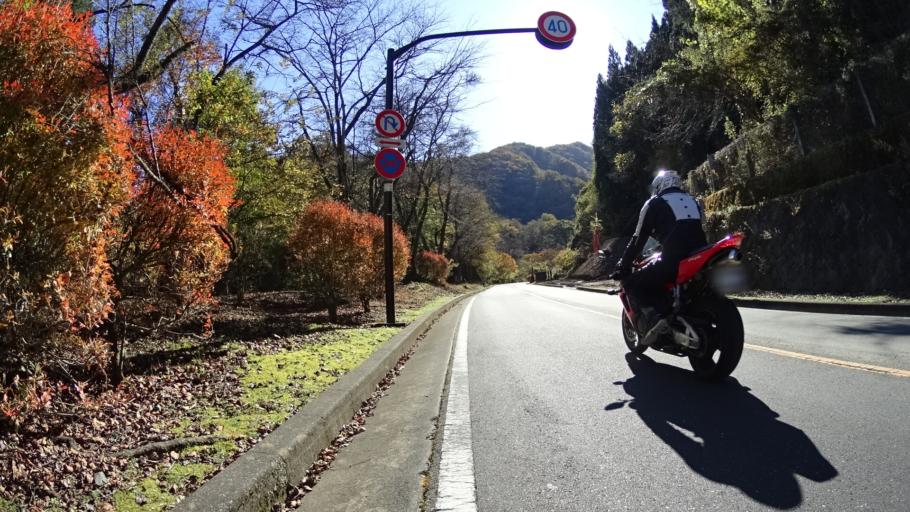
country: JP
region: Yamanashi
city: Uenohara
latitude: 35.7628
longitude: 139.0216
